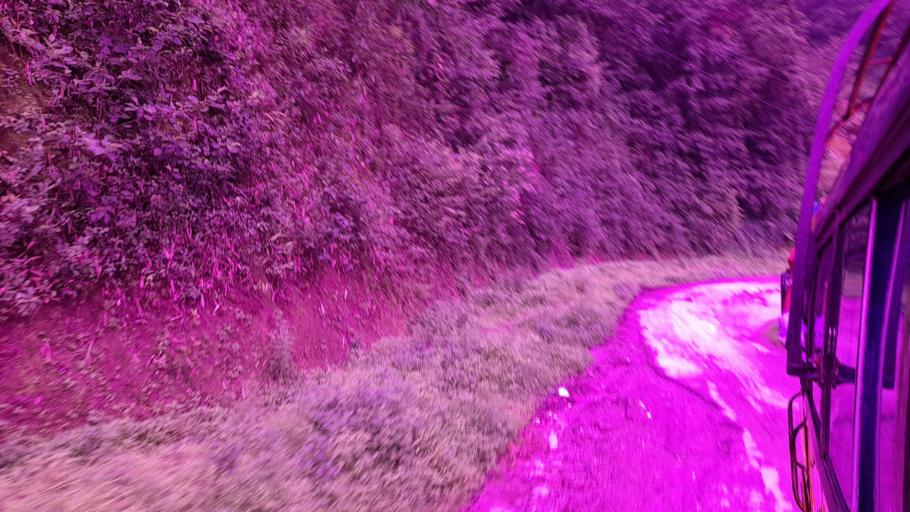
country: NP
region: Central Region
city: Kirtipur
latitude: 27.8129
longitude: 85.2151
